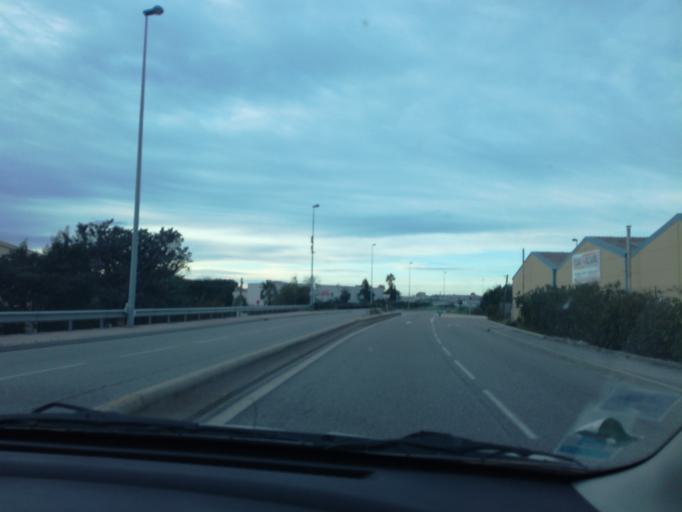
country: FR
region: Provence-Alpes-Cote d'Azur
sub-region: Departement du Var
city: La Farlede
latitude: 43.1580
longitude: 6.0502
